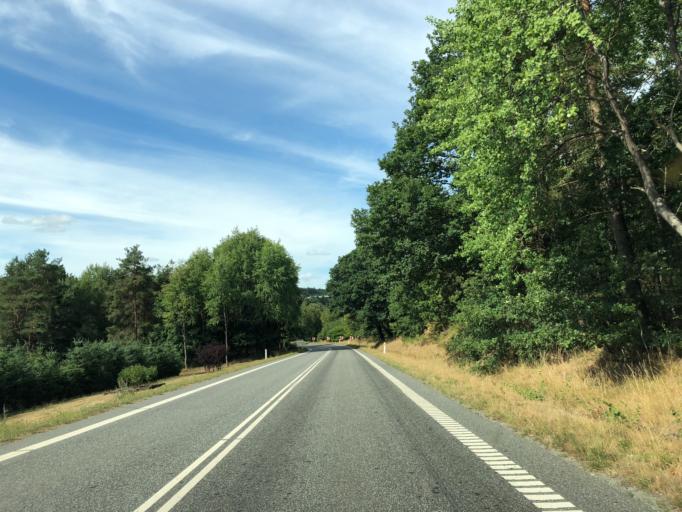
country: DK
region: Central Jutland
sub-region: Silkeborg Kommune
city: Silkeborg
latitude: 56.1401
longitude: 9.4165
